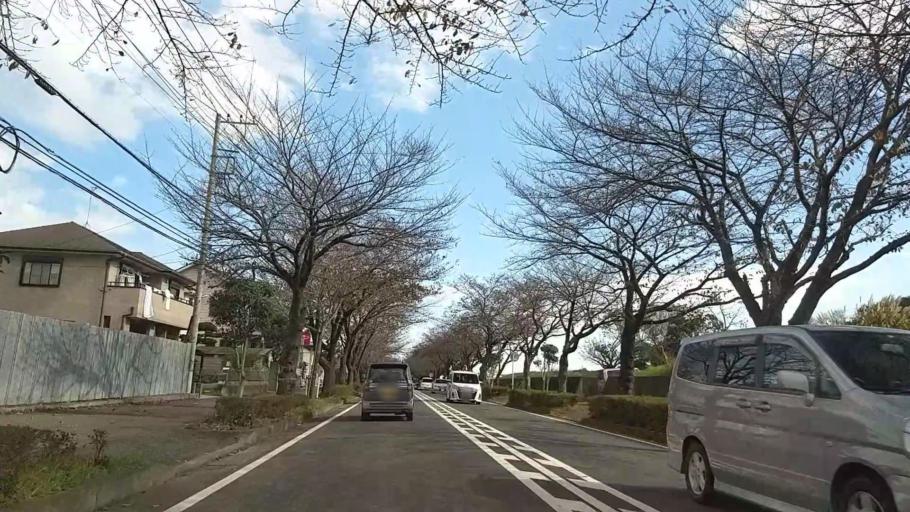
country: JP
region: Kanagawa
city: Hadano
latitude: 35.3622
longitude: 139.2199
